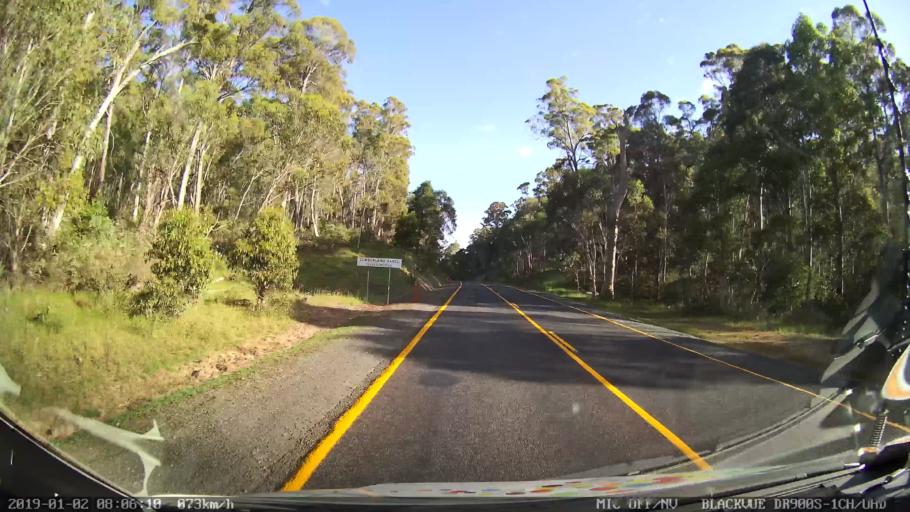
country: AU
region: New South Wales
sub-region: Tumut Shire
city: Tumut
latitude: -35.6430
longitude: 148.3872
